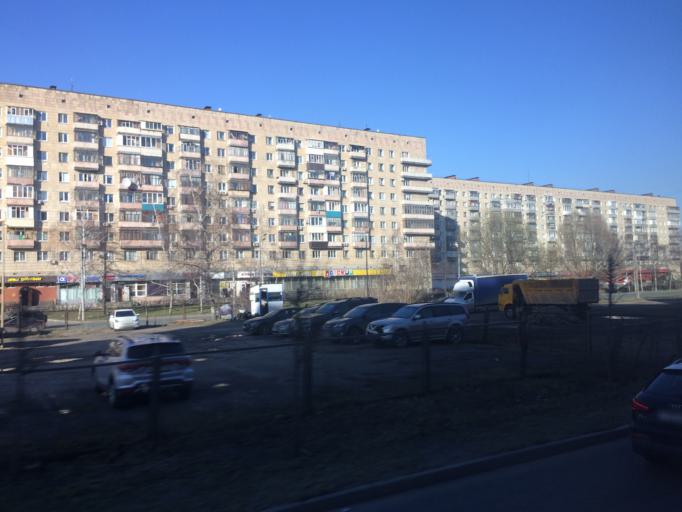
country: RU
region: Tatarstan
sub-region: Gorod Kazan'
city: Kazan
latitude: 55.8208
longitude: 49.0507
